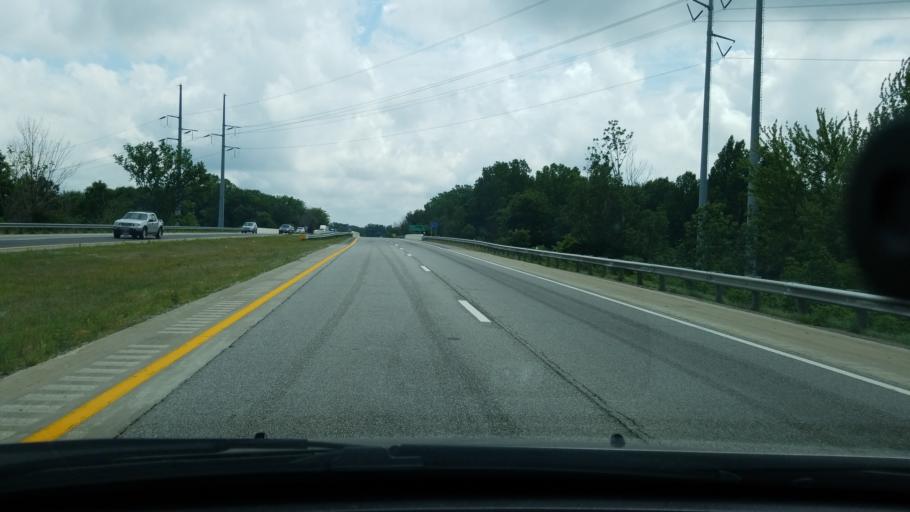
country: US
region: Ohio
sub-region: Lorain County
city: Lorain
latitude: 41.4086
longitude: -82.1542
